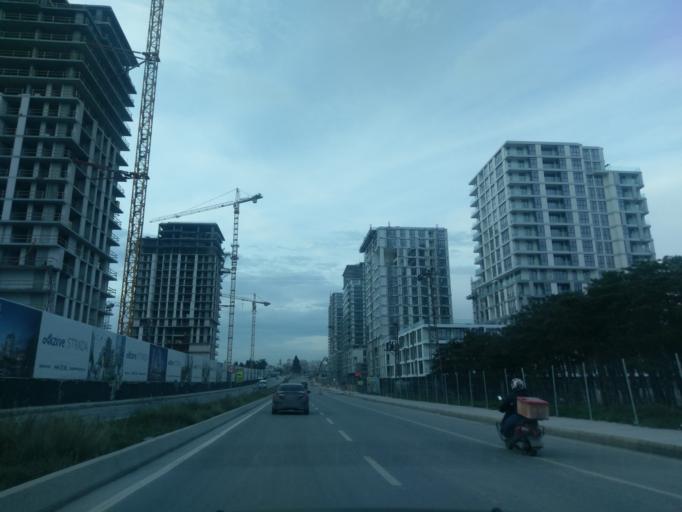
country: TR
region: Istanbul
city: Esenyurt
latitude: 41.0735
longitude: 28.6594
